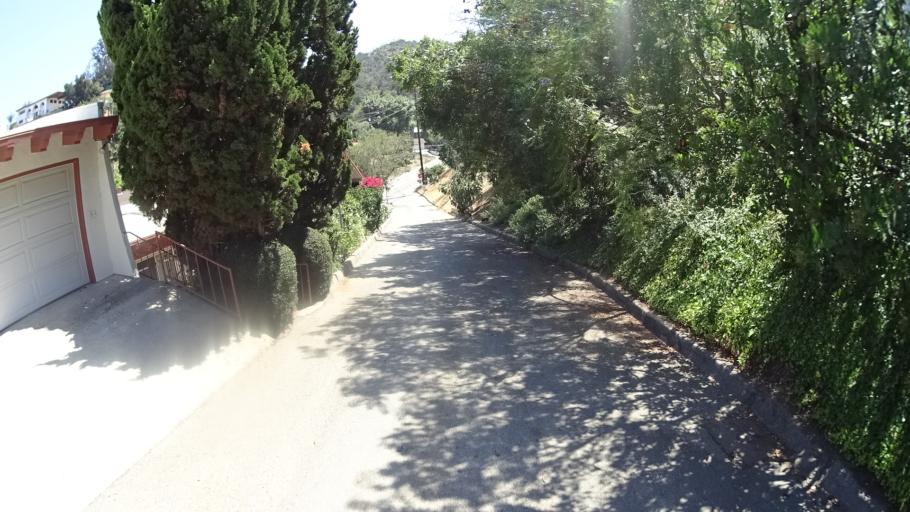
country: US
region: California
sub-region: Los Angeles County
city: Sherman Oaks
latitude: 34.1356
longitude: -118.4135
